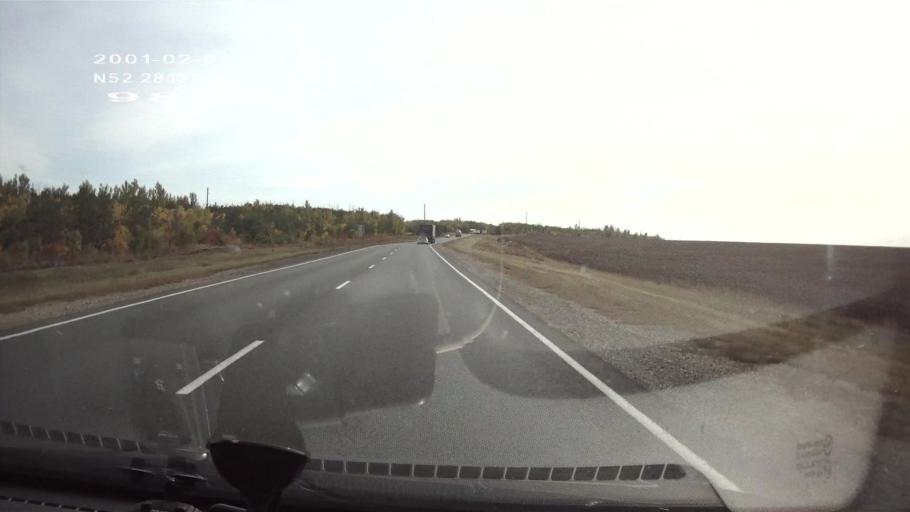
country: RU
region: Saratov
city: Alekseyevka
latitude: 52.2817
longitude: 47.9324
